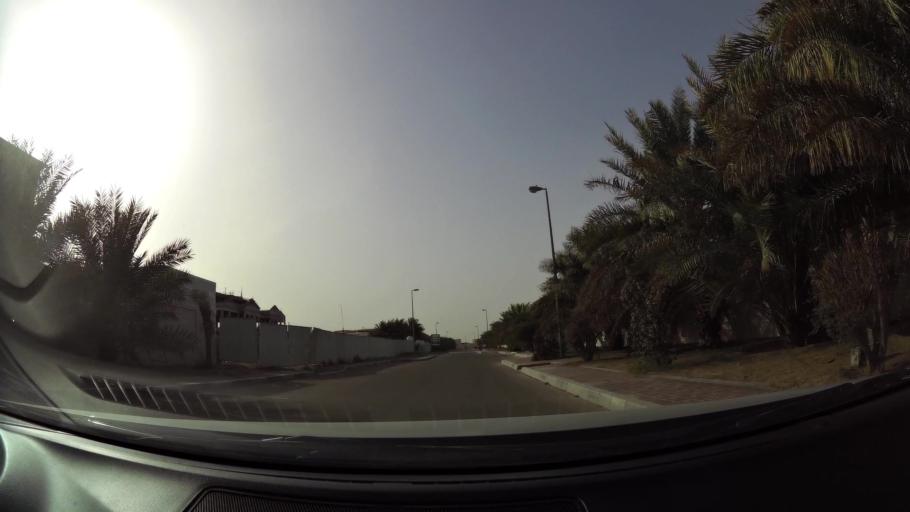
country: AE
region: Abu Dhabi
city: Al Ain
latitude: 24.2189
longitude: 55.6532
